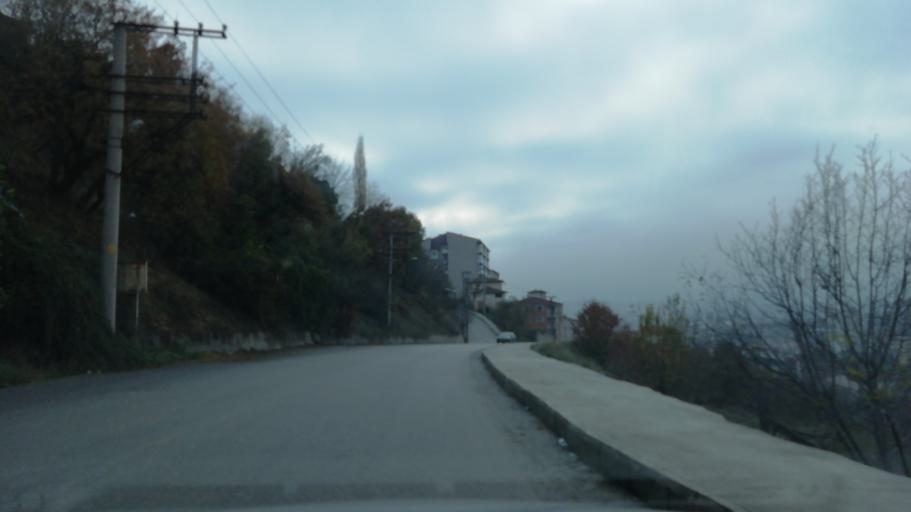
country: TR
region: Karabuk
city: Karabuk
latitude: 41.2118
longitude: 32.6286
